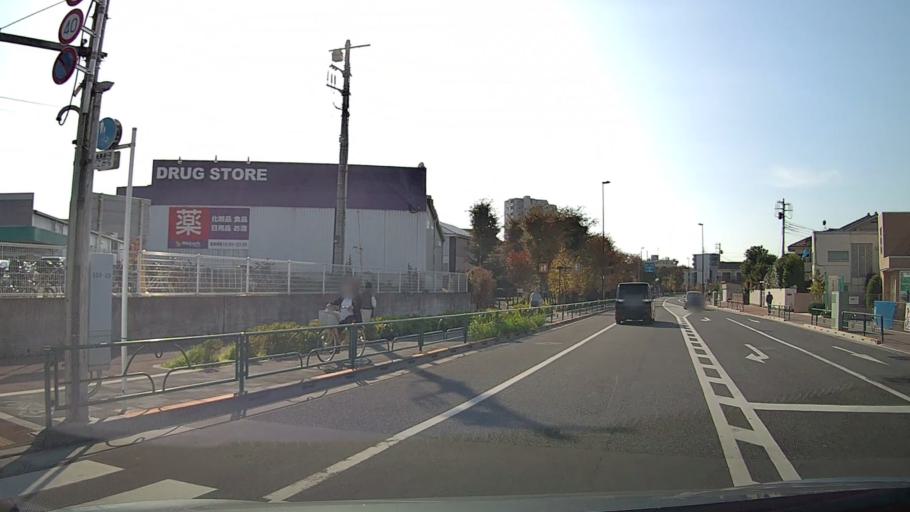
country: JP
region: Tokyo
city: Musashino
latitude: 35.7234
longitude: 139.5915
